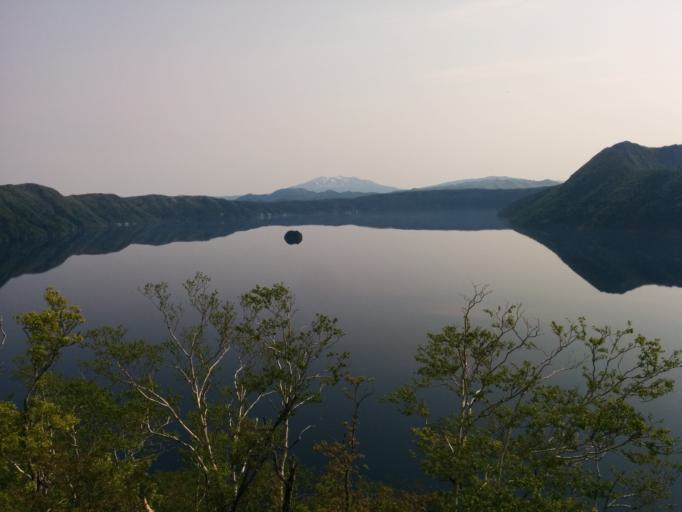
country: JP
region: Hokkaido
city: Bihoro
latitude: 43.5571
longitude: 144.5068
